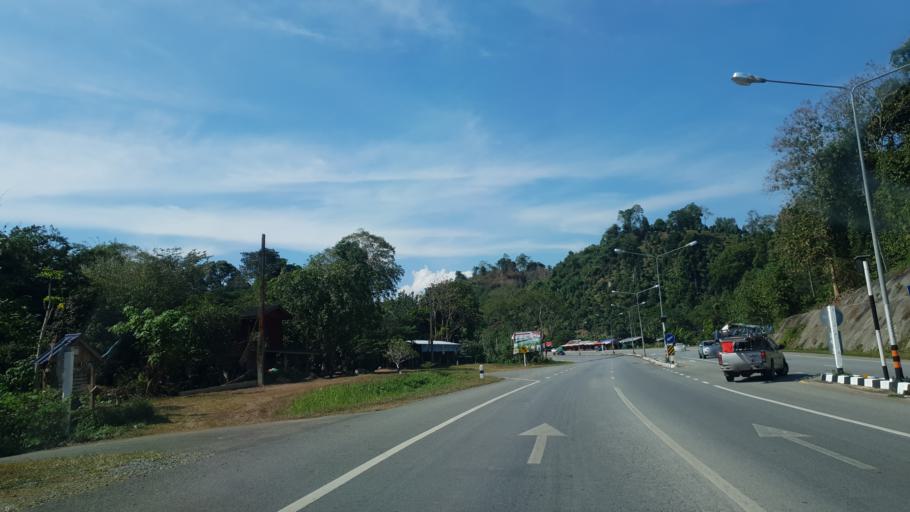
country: TH
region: Phrae
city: Den Chai
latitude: 17.8182
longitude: 100.0983
